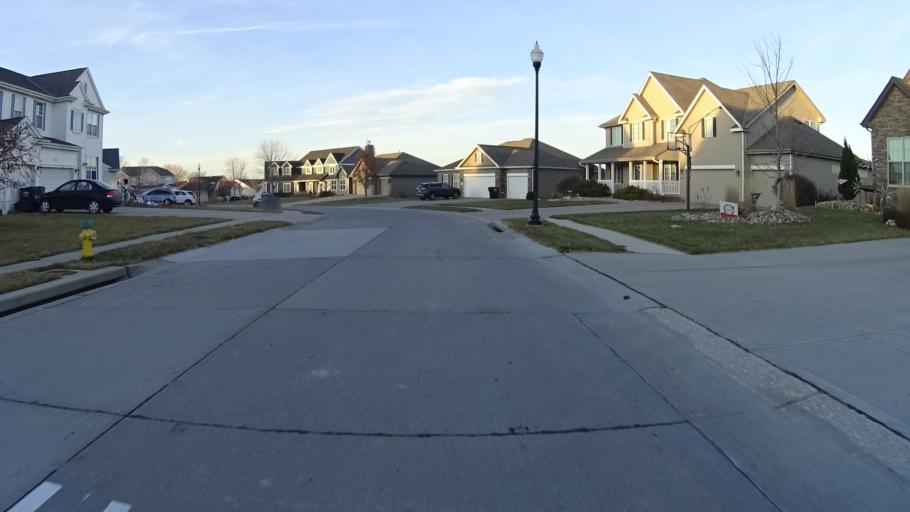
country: US
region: Nebraska
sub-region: Sarpy County
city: Papillion
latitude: 41.1305
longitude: -96.0685
